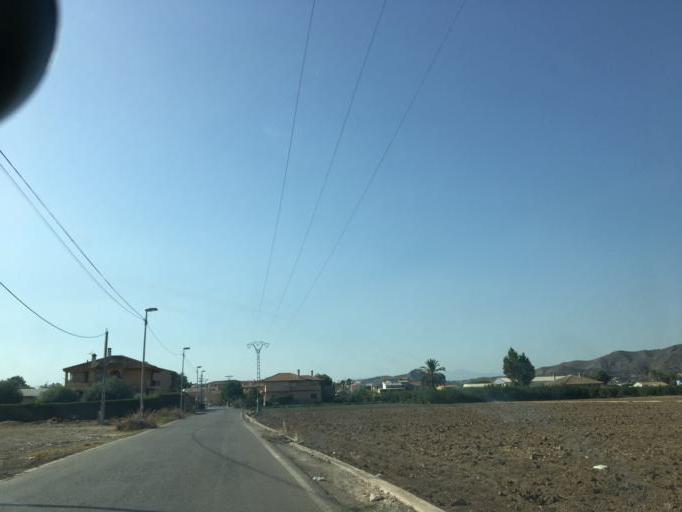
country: ES
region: Murcia
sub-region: Murcia
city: Santomera
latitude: 38.0343
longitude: -1.0723
